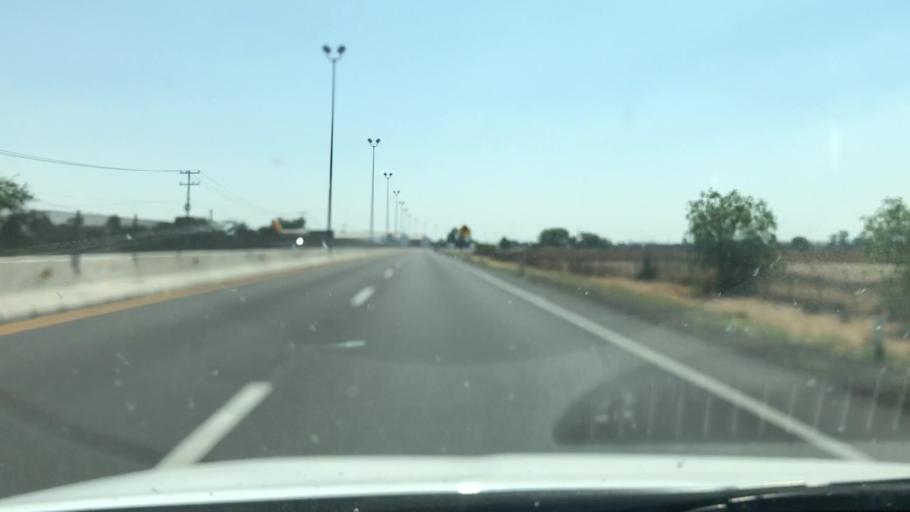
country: MX
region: Guanajuato
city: Abasolo
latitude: 20.4629
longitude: -101.5216
